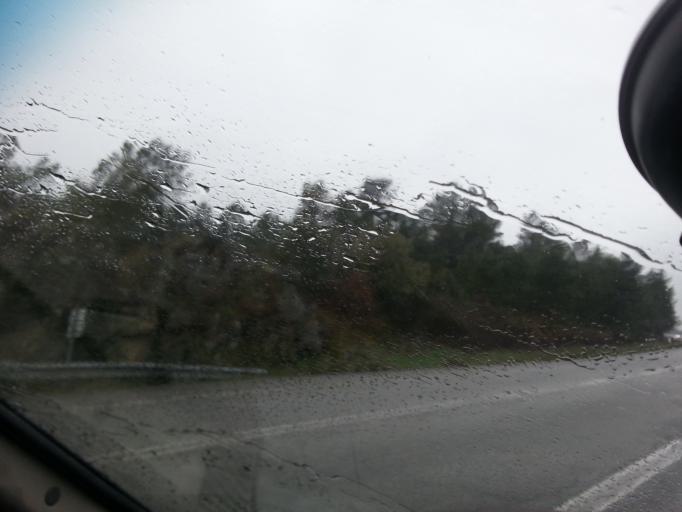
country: PT
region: Guarda
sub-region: Fornos de Algodres
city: Fornos de Algodres
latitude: 40.6118
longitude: -7.5936
